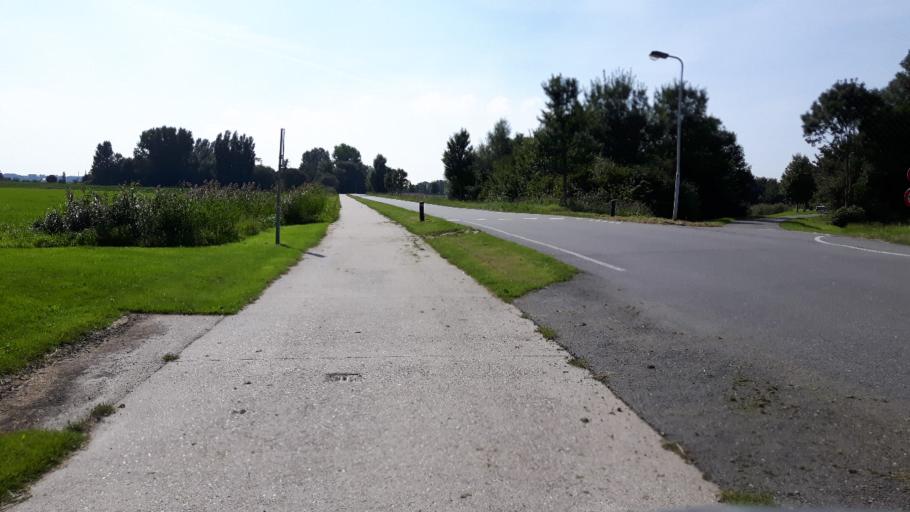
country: NL
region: Friesland
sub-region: Gemeente Franekeradeel
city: Tzummarum
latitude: 53.2153
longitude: 5.5681
